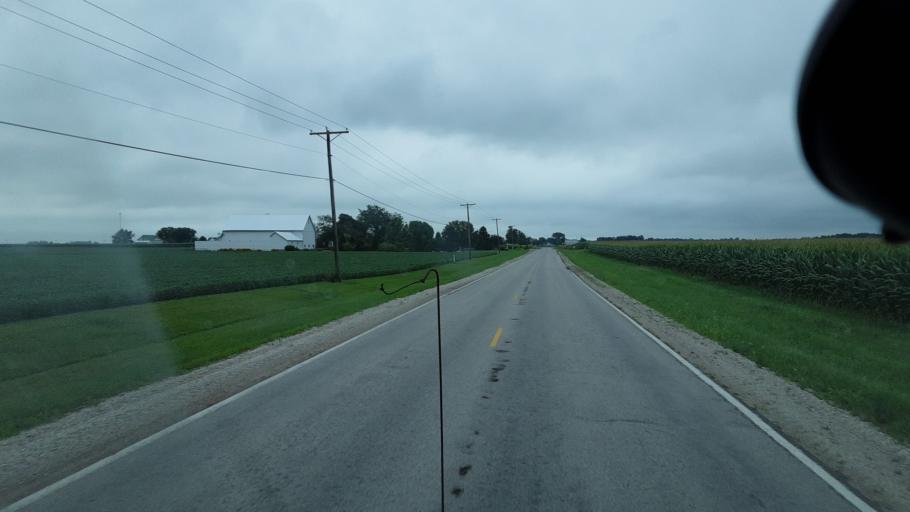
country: US
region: Indiana
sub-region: Wells County
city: Bluffton
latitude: 40.7496
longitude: -85.0902
